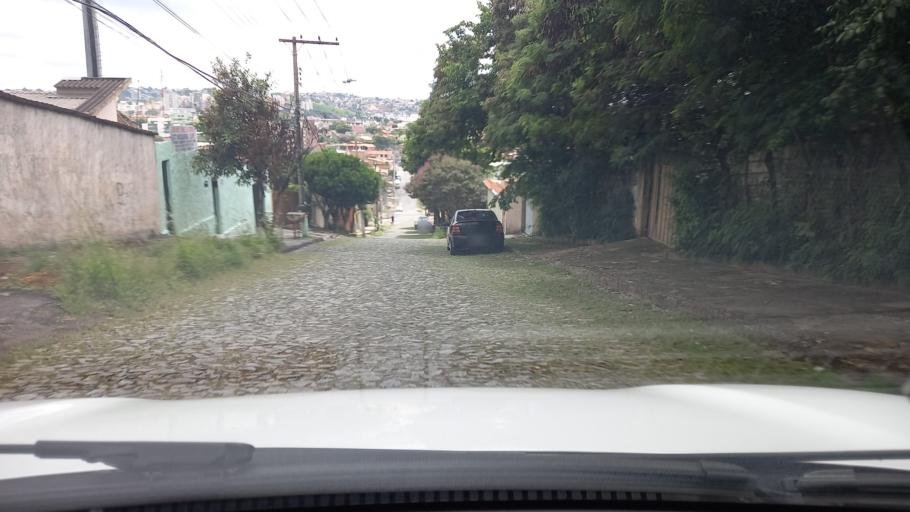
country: BR
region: Minas Gerais
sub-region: Contagem
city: Contagem
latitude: -19.9010
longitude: -44.0118
